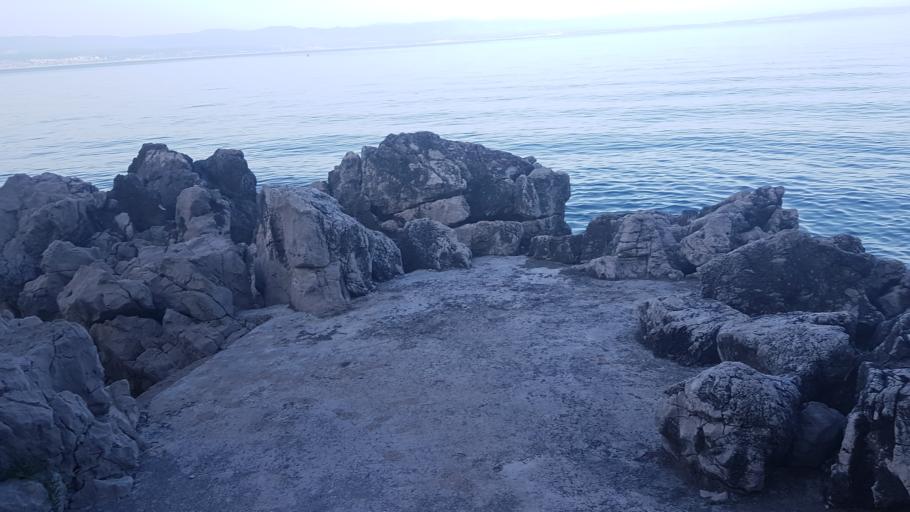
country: HR
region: Istarska
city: Lovran
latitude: 45.2286
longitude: 14.2547
